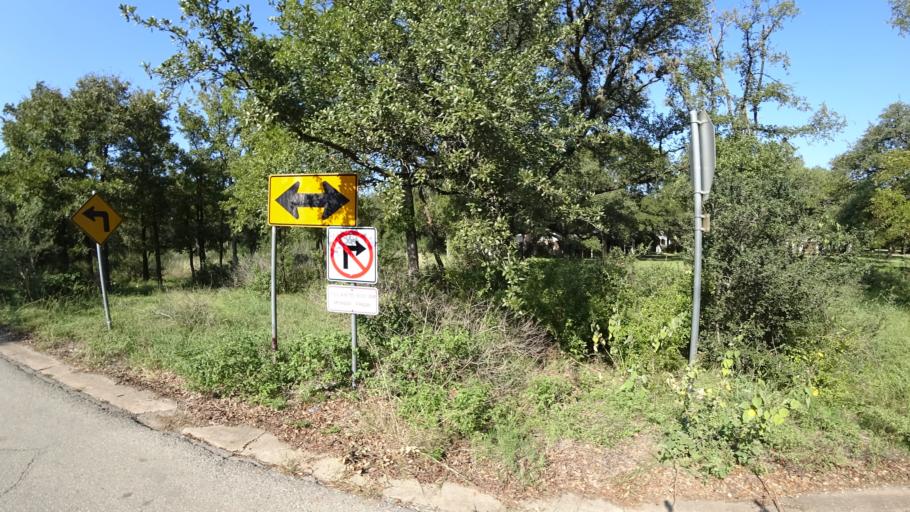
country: US
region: Texas
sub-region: Travis County
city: West Lake Hills
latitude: 30.2857
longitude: -97.8042
